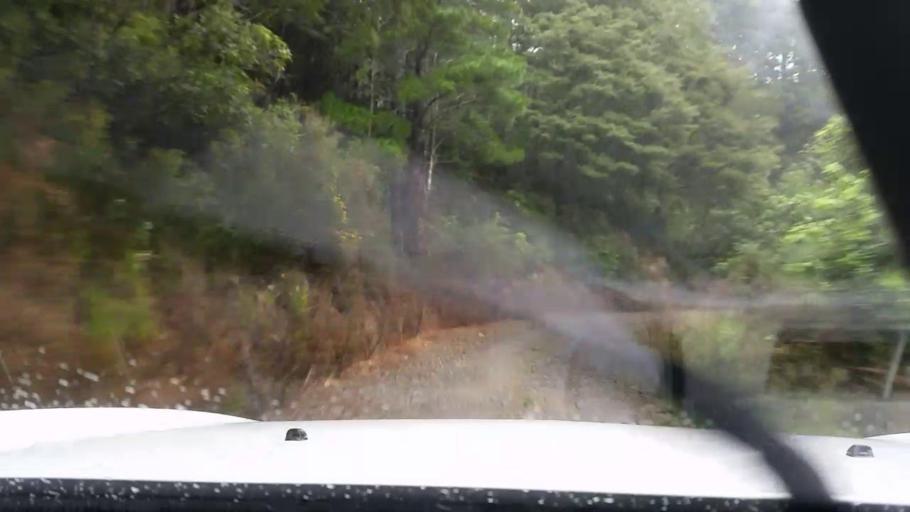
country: NZ
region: Wellington
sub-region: Masterton District
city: Masterton
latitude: -41.1587
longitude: 175.8024
